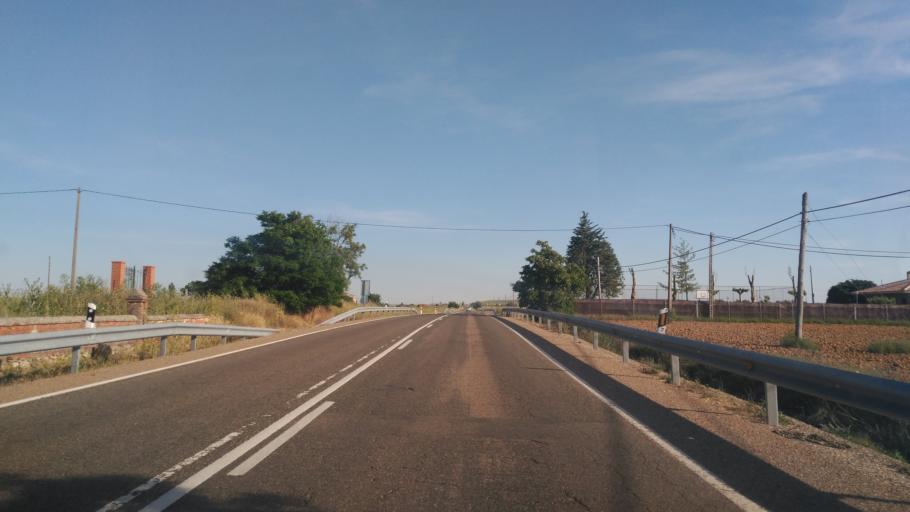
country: ES
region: Castille and Leon
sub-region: Provincia de Zamora
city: Morales del Vino
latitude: 41.4395
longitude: -5.7300
